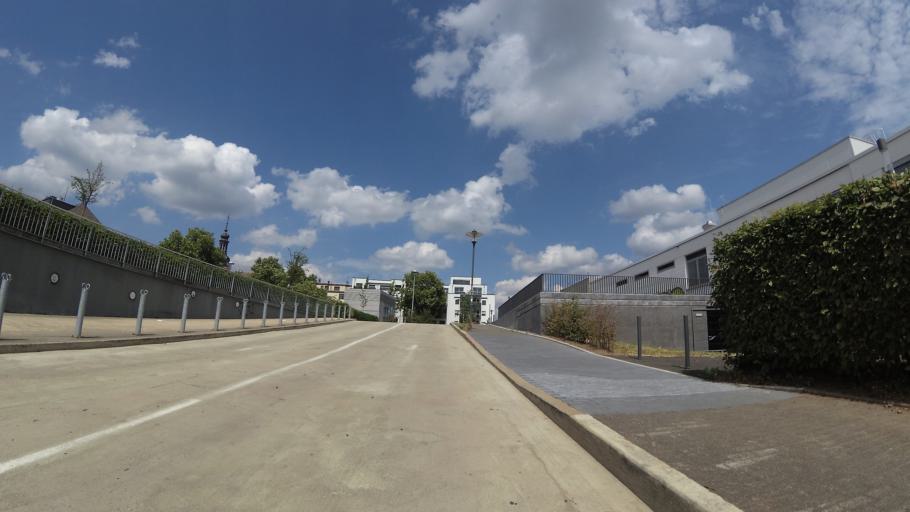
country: DE
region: Saarland
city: Saarbrucken
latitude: 49.2303
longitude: 6.9972
